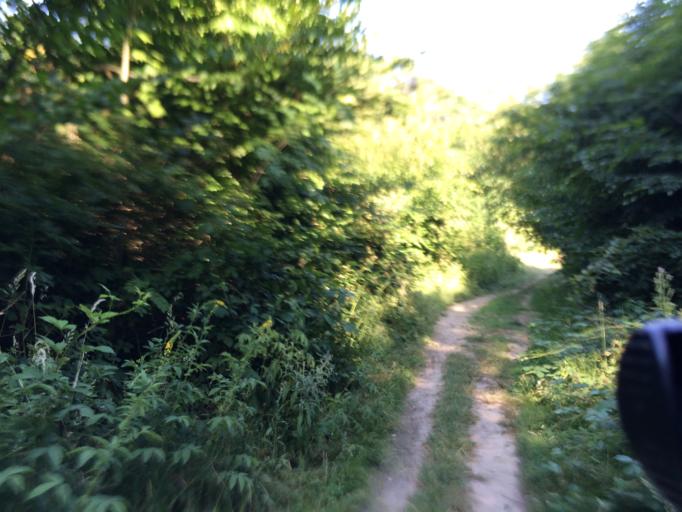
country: FR
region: Ile-de-France
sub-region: Departement de l'Essonne
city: Soisy-sur-Seine
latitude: 48.6507
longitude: 2.4705
